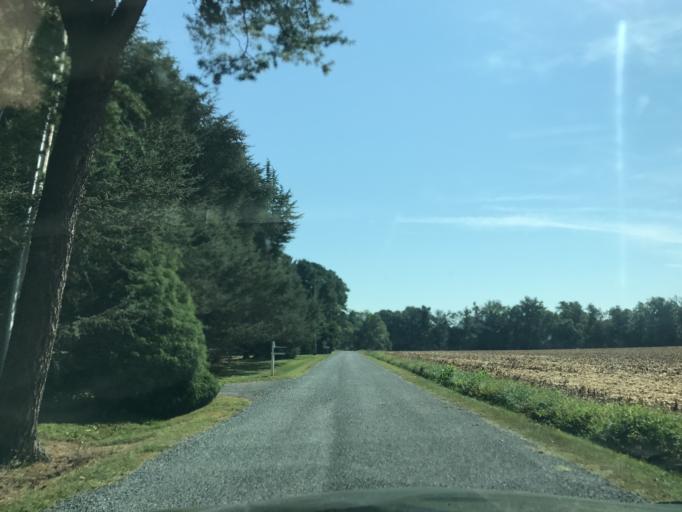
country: US
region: Maryland
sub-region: Queen Anne's County
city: Kingstown
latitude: 39.3691
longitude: -75.9570
